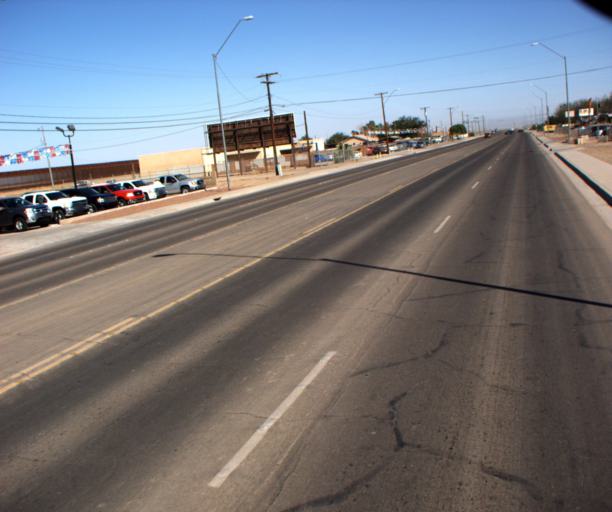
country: US
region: Arizona
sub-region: Yuma County
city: San Luis
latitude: 32.5594
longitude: -114.7846
